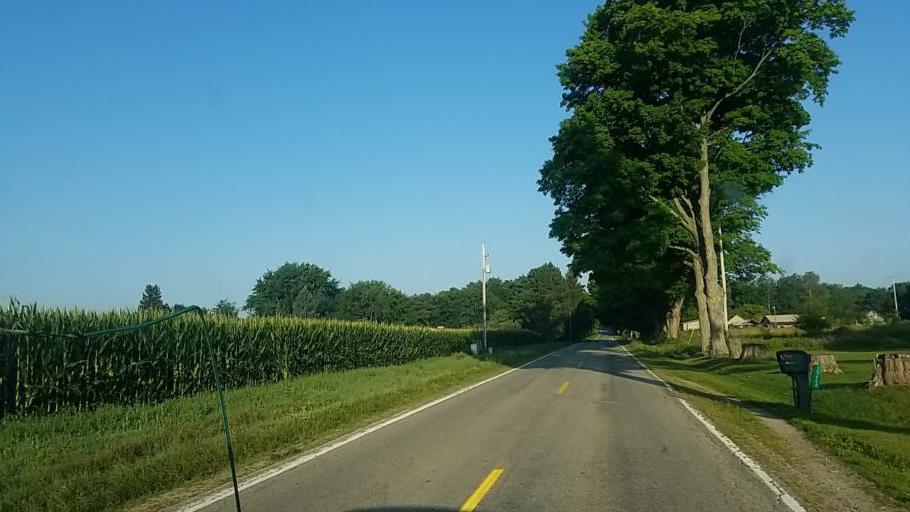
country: US
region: Michigan
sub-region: Montcalm County
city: Howard City
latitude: 43.3594
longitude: -85.3961
